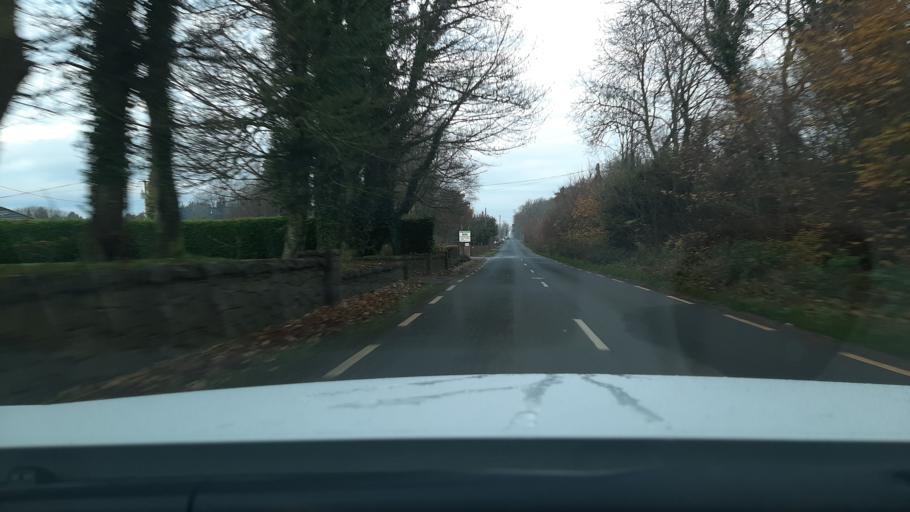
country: IE
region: Leinster
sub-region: Kildare
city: Rathangan
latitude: 53.2372
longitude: -7.0104
